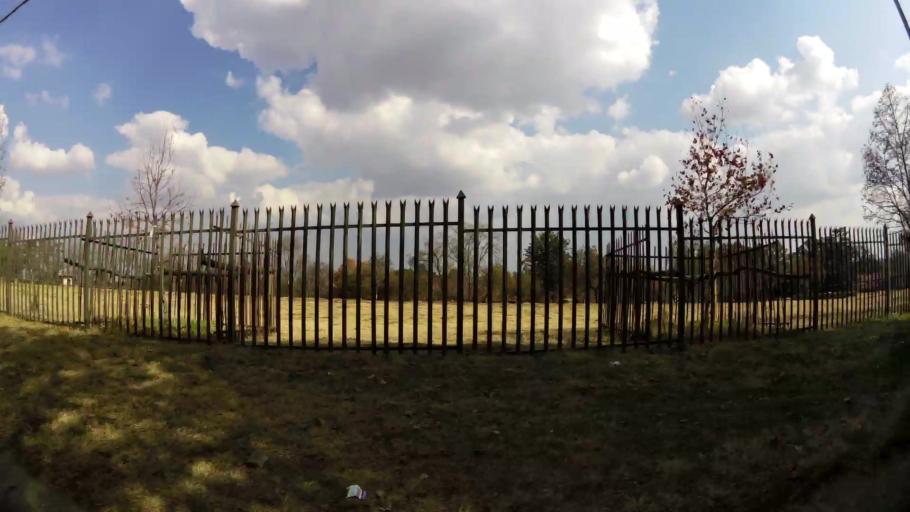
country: ZA
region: Gauteng
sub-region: City of Tshwane Metropolitan Municipality
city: Centurion
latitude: -25.8772
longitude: 28.2145
